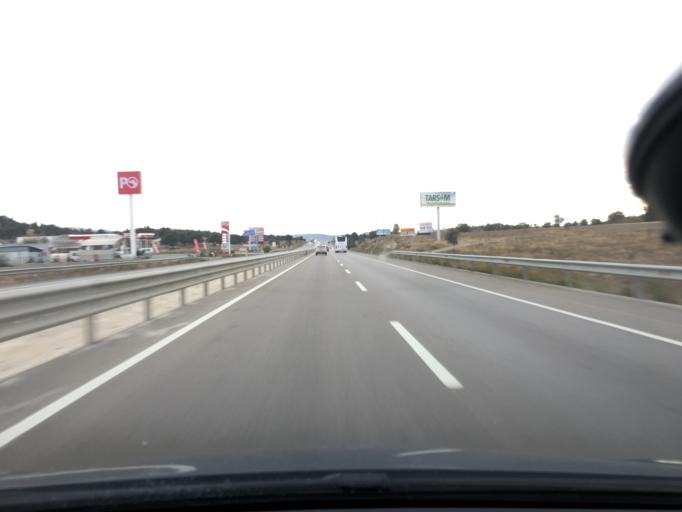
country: TR
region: Afyonkarahisar
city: Sincanli
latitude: 38.6534
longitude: 30.3186
